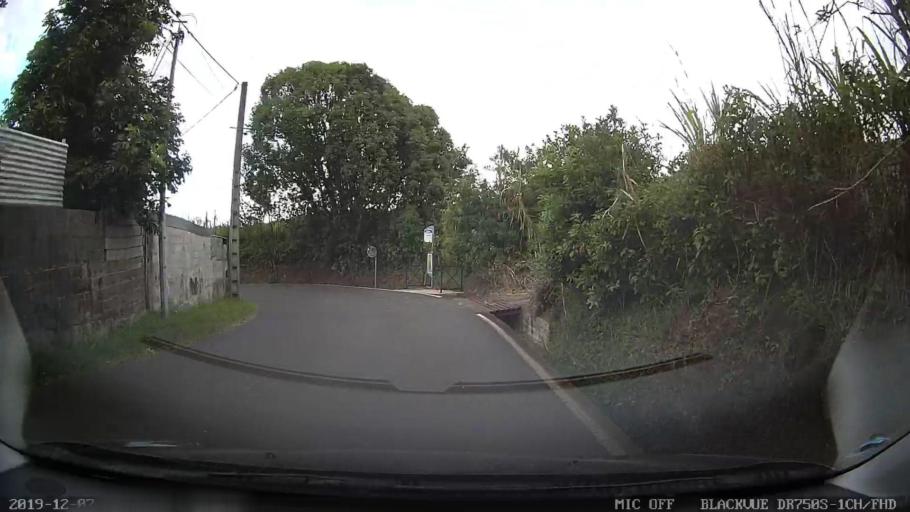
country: RE
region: Reunion
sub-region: Reunion
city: Sainte-Marie
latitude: -20.9376
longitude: 55.5340
